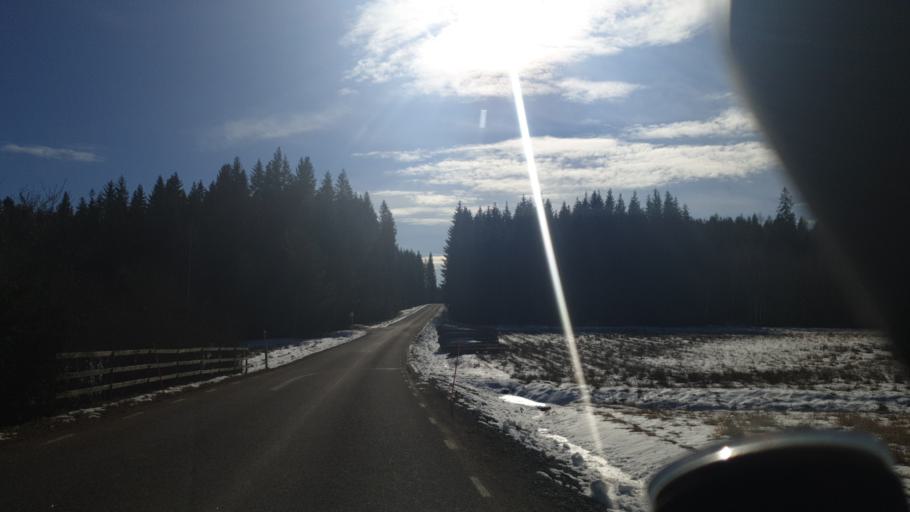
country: SE
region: Vaermland
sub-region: Grums Kommun
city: Grums
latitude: 59.5008
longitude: 12.8748
